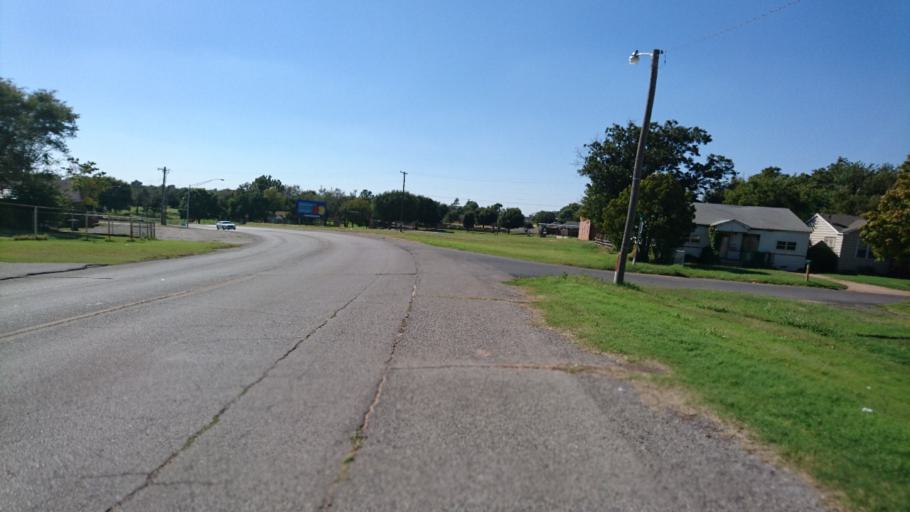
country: US
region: Oklahoma
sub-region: Custer County
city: Clinton
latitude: 35.5066
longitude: -98.9704
